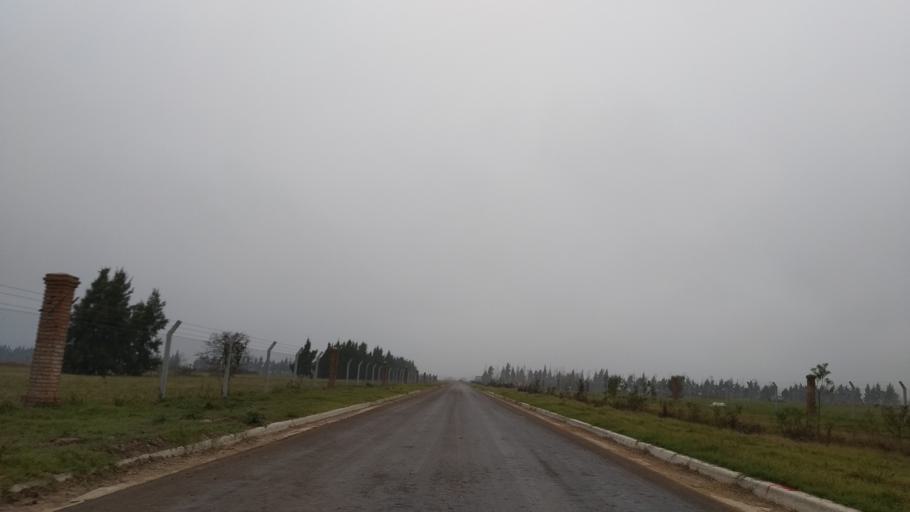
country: AR
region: Santa Fe
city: Funes
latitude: -32.9435
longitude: -60.7689
